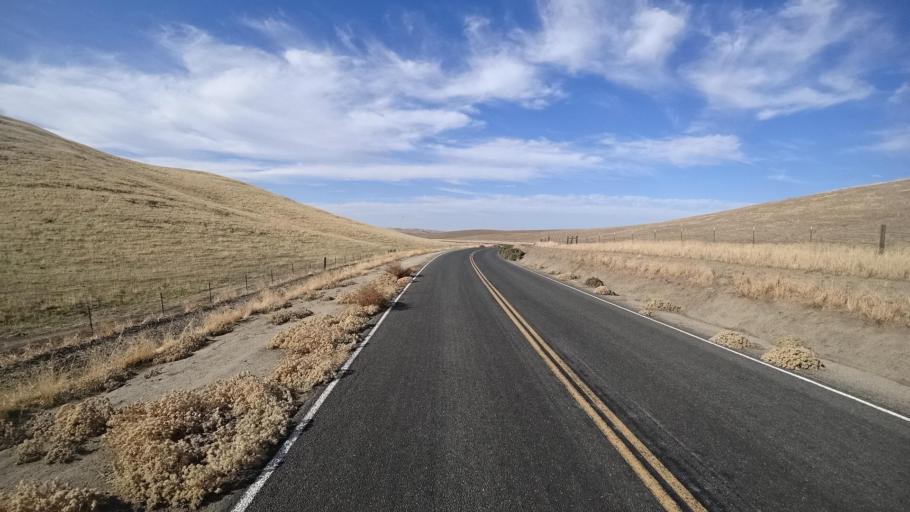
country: US
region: California
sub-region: Kern County
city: Oildale
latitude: 35.6114
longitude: -118.9363
